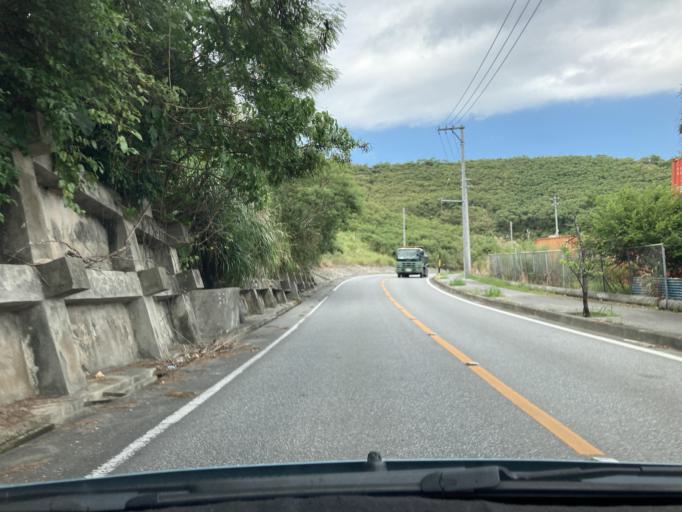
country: JP
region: Okinawa
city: Ginowan
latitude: 26.2621
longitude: 127.7837
